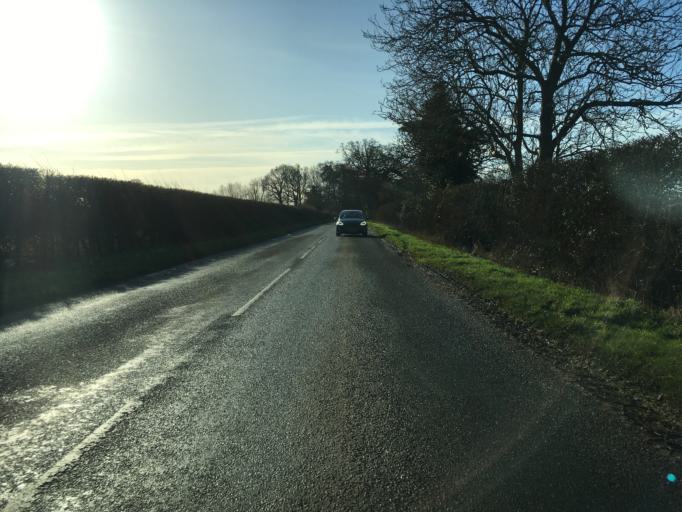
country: GB
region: England
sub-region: Warwickshire
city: Wellesbourne Mountford
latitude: 52.2130
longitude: -1.6097
